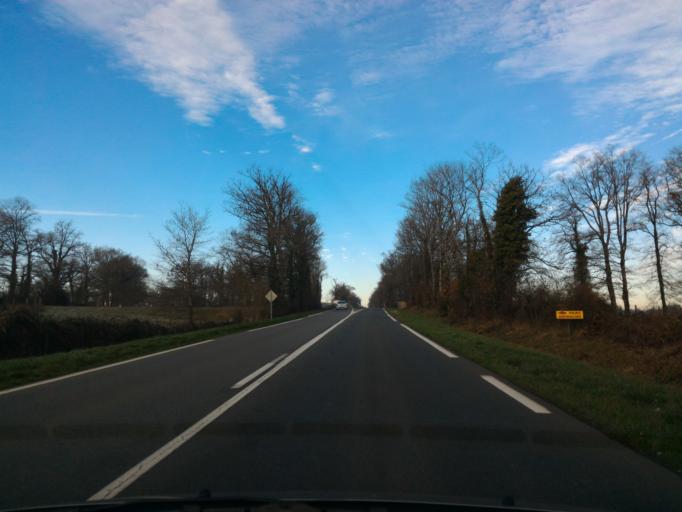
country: FR
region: Poitou-Charentes
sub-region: Departement de la Charente
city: Confolens
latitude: 46.0306
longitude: 0.6434
